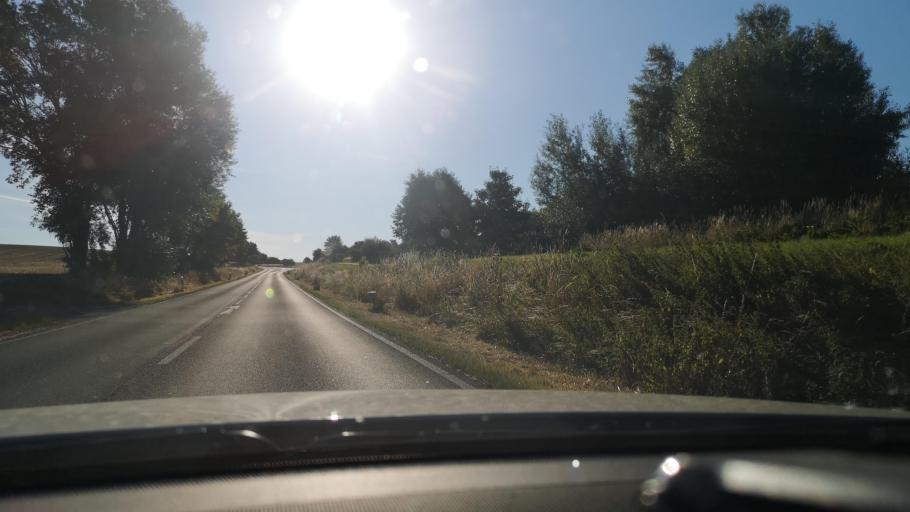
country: DE
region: Thuringia
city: Apolda
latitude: 51.0246
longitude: 11.5382
